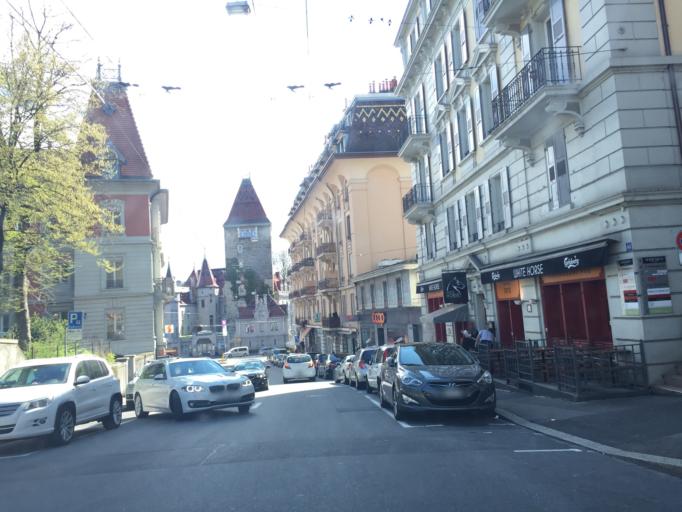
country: CH
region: Vaud
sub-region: Lausanne District
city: Lausanne
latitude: 46.5081
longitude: 6.6273
